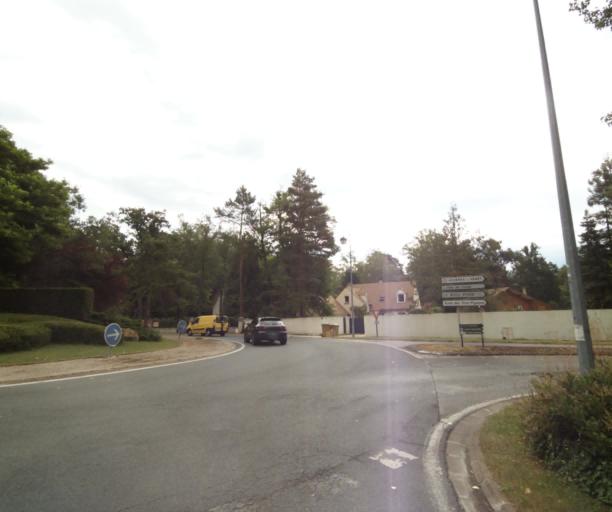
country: FR
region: Ile-de-France
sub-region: Departement de Seine-et-Marne
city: Arbonne-la-Foret
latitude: 48.4089
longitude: 2.5629
